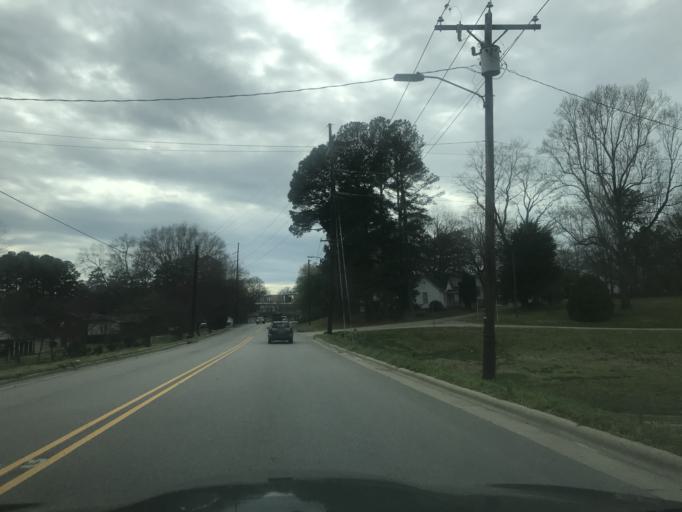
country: US
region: North Carolina
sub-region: Franklin County
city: Franklinton
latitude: 36.1015
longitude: -78.4533
